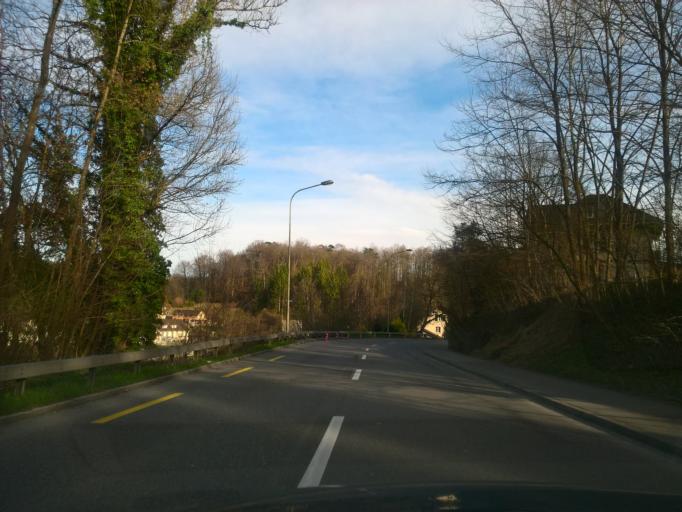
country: CH
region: Zurich
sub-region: Bezirk Buelach
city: Rorbas
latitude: 47.5278
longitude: 8.5784
